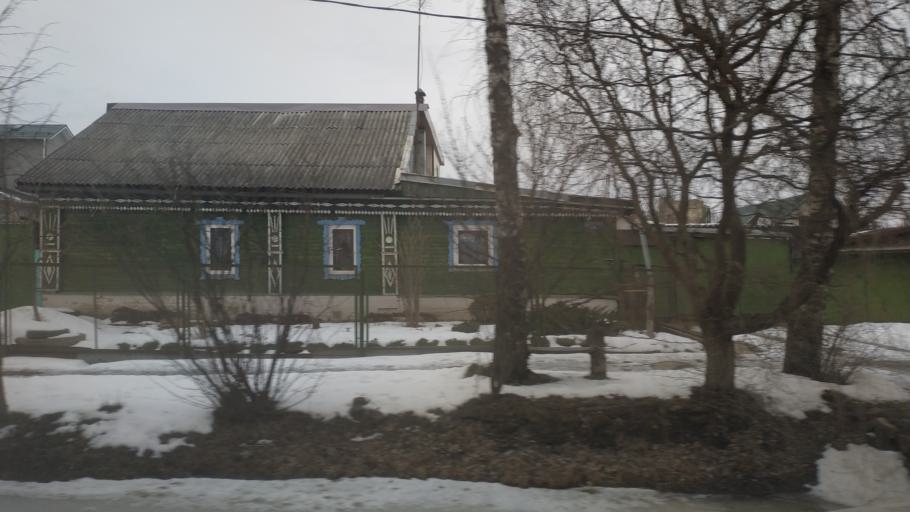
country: RU
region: Tverskaya
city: Tver
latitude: 56.8914
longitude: 35.8656
